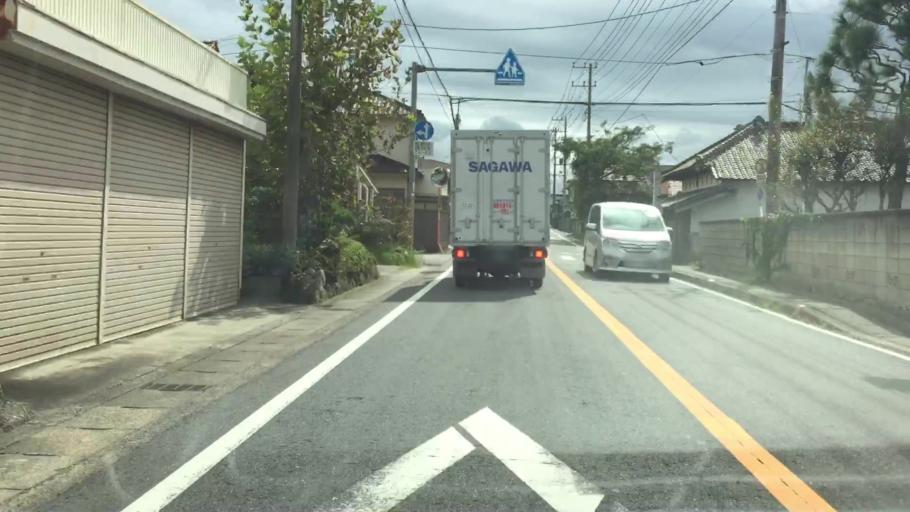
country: JP
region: Ibaraki
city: Ryugasaki
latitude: 35.8480
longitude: 140.1411
